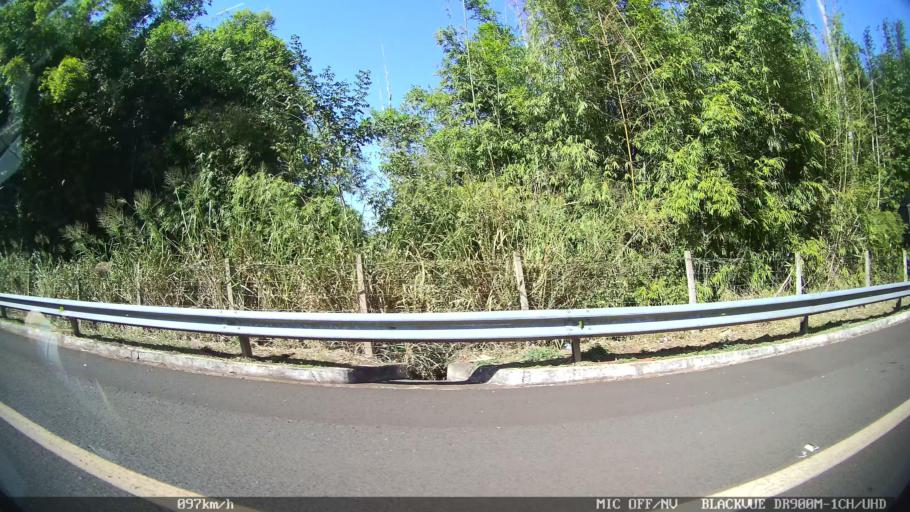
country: BR
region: Sao Paulo
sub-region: Batatais
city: Batatais
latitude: -20.7314
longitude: -47.5240
